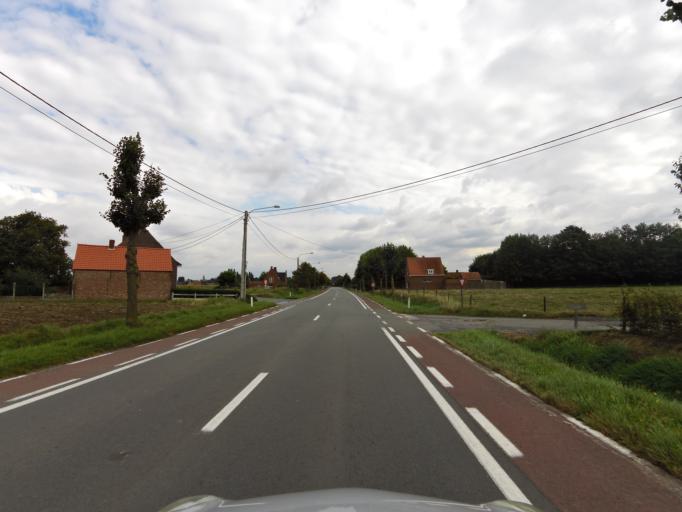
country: BE
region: Flanders
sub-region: Provincie West-Vlaanderen
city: Pittem
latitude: 50.9958
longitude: 3.2455
